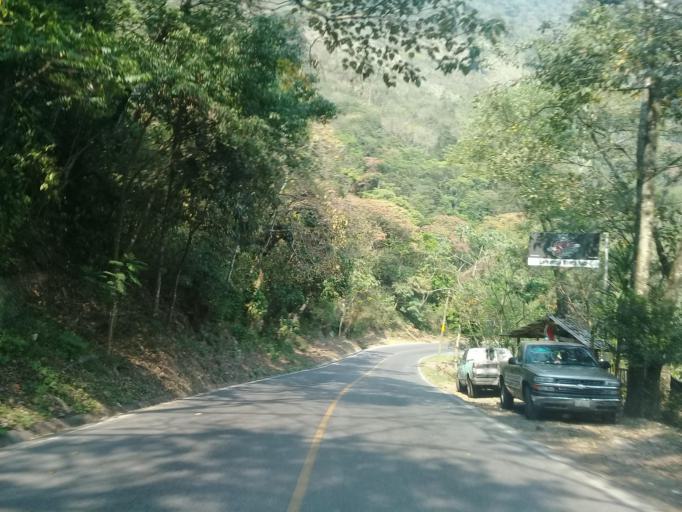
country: MX
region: Veracruz
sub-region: Ixtaczoquitlan
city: Campo Chico
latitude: 18.8409
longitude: -97.0251
